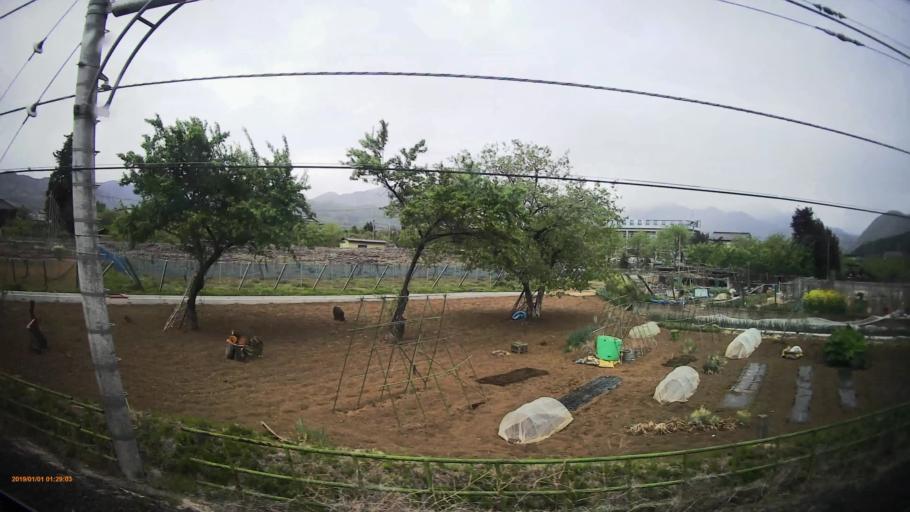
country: JP
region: Yamanashi
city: Enzan
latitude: 35.7020
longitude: 138.7168
